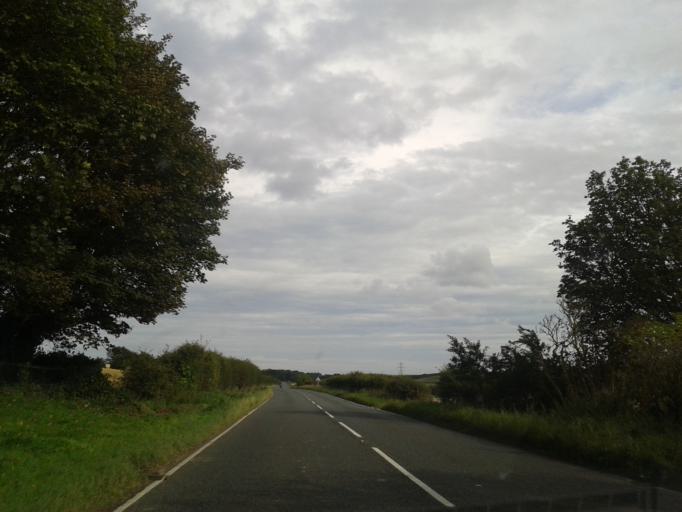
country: GB
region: Scotland
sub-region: Aberdeenshire
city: Whitehills
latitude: 57.6546
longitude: -2.6129
